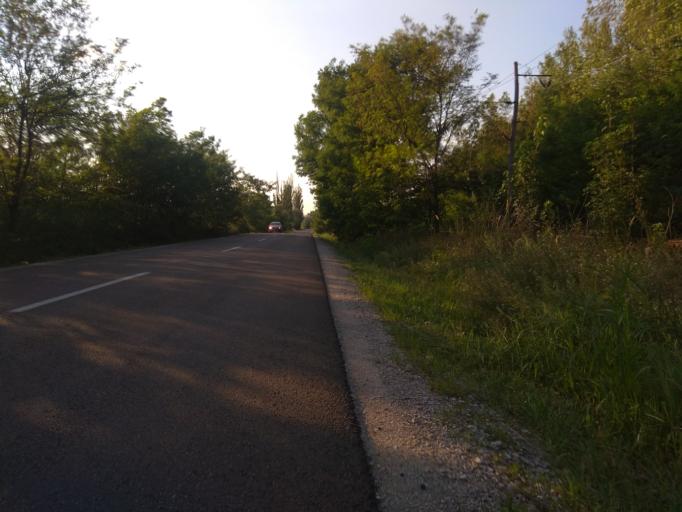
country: HU
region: Borsod-Abauj-Zemplen
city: Nyekladhaza
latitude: 47.9660
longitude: 20.8581
